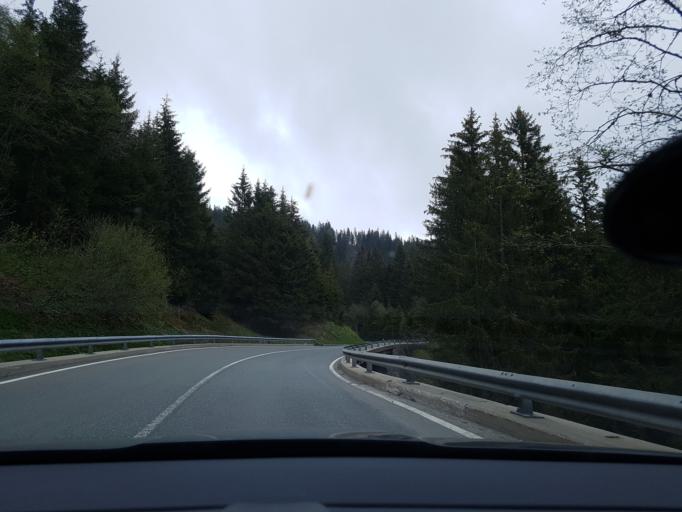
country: AT
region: Salzburg
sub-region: Politischer Bezirk Zell am See
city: Krimml
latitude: 47.2246
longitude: 12.1564
